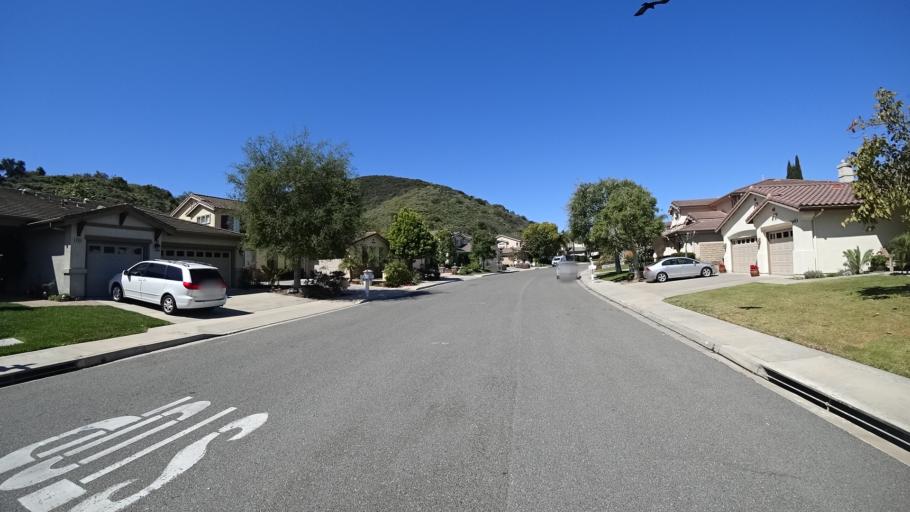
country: US
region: California
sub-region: Ventura County
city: Casa Conejo
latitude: 34.1646
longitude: -118.9723
